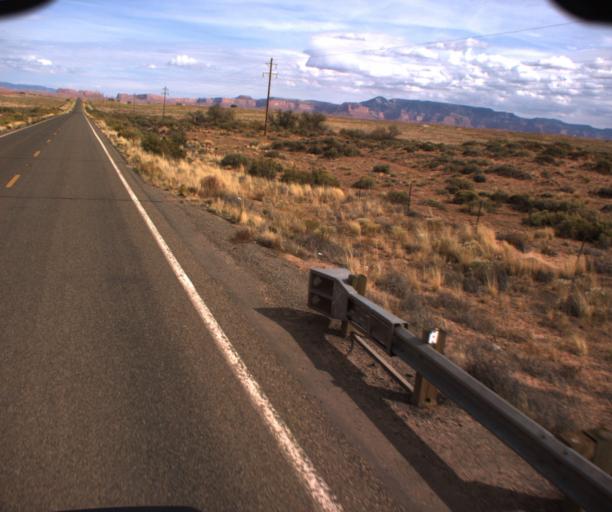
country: US
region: Arizona
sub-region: Apache County
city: Many Farms
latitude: 36.4942
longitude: -109.4917
